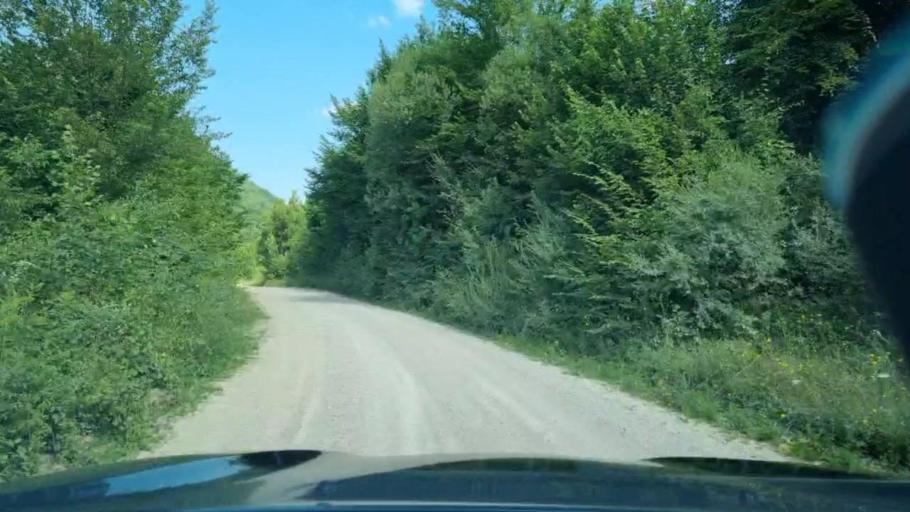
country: BA
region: Federation of Bosnia and Herzegovina
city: Peci
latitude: 44.5893
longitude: 16.8305
